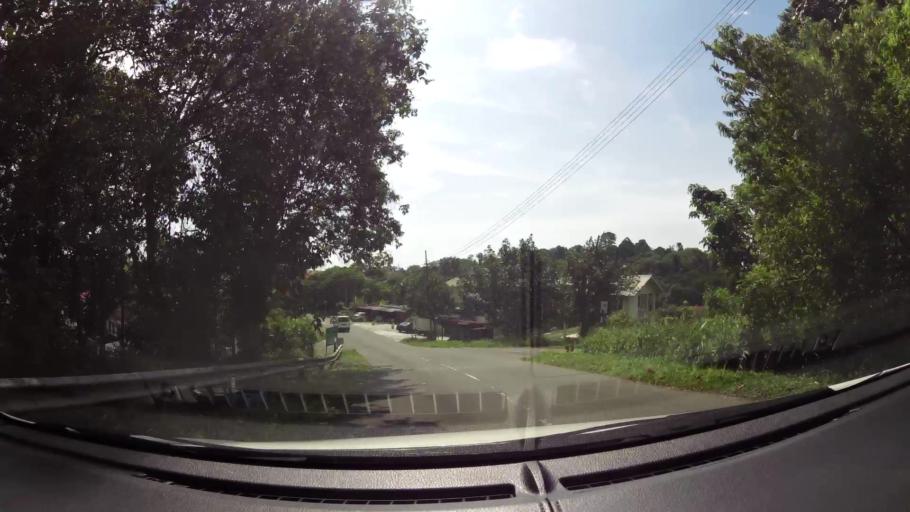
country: BN
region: Brunei and Muara
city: Bandar Seri Begawan
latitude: 4.9562
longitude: 114.9511
